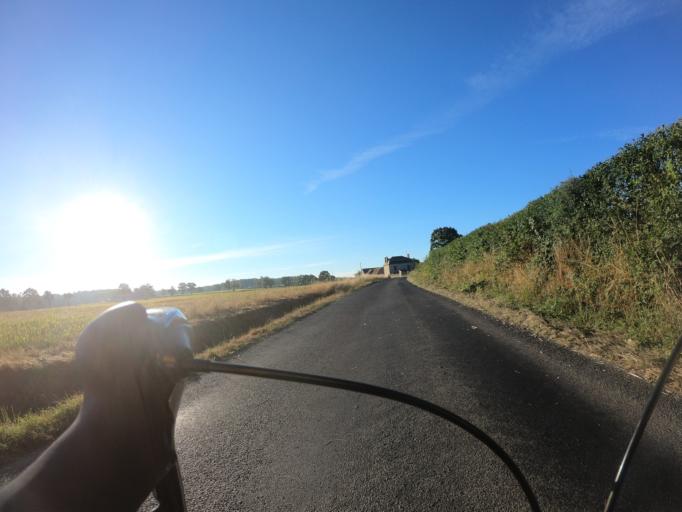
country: FR
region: Lower Normandy
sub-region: Departement de l'Orne
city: Magny-le-Desert
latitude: 48.5398
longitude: -0.2981
